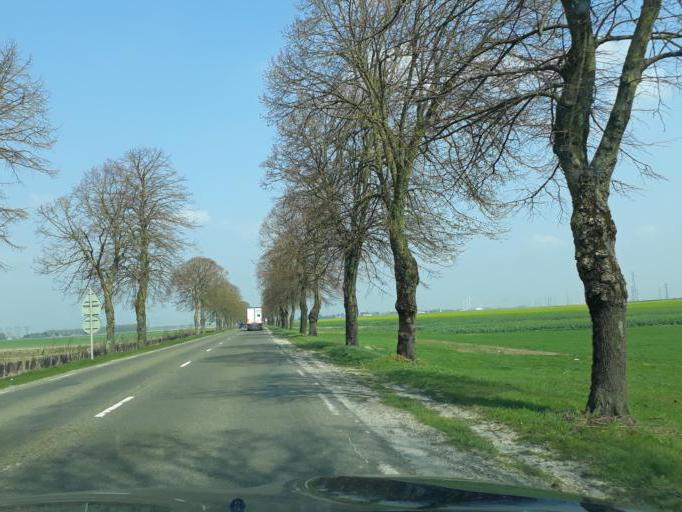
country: FR
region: Centre
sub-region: Departement du Loiret
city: Artenay
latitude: 48.0898
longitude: 1.8655
